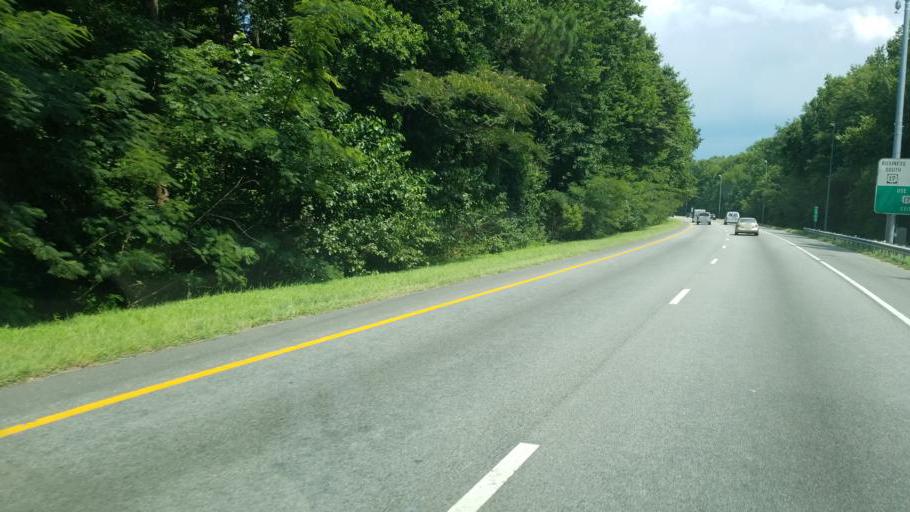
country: US
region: Virginia
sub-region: City of Portsmouth
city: Portsmouth Heights
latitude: 36.7594
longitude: -76.3546
